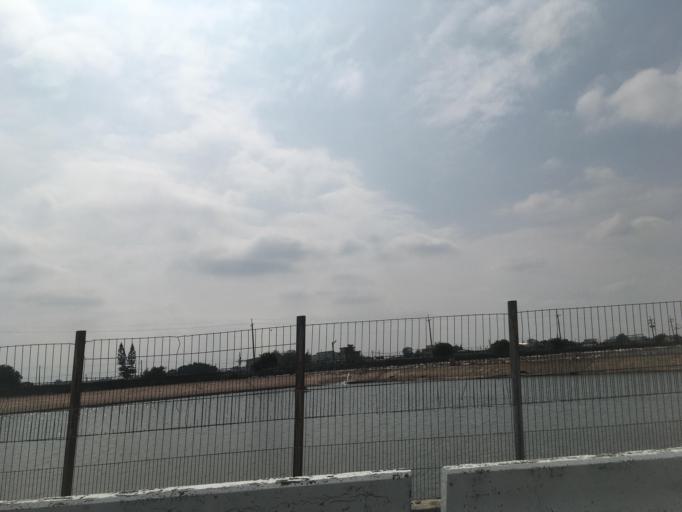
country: TW
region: Taiwan
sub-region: Yunlin
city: Douliu
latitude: 23.6948
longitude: 120.4552
